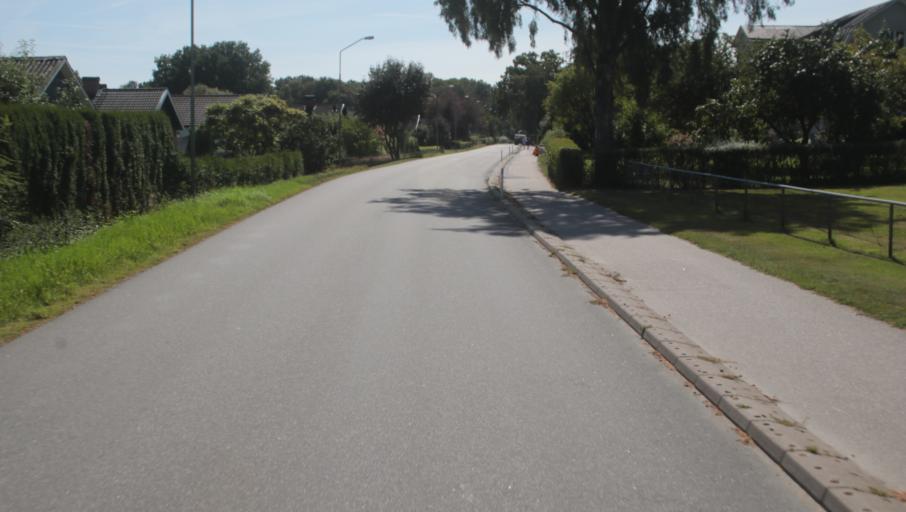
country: SE
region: Blekinge
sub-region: Karlshamns Kommun
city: Karlshamn
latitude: 56.2008
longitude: 14.8265
